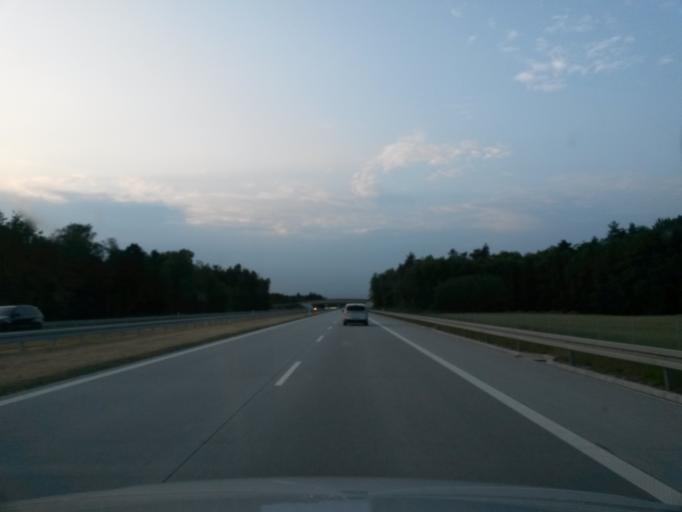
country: PL
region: Lodz Voivodeship
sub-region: Powiat sieradzki
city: Zloczew
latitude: 51.4323
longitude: 18.6460
